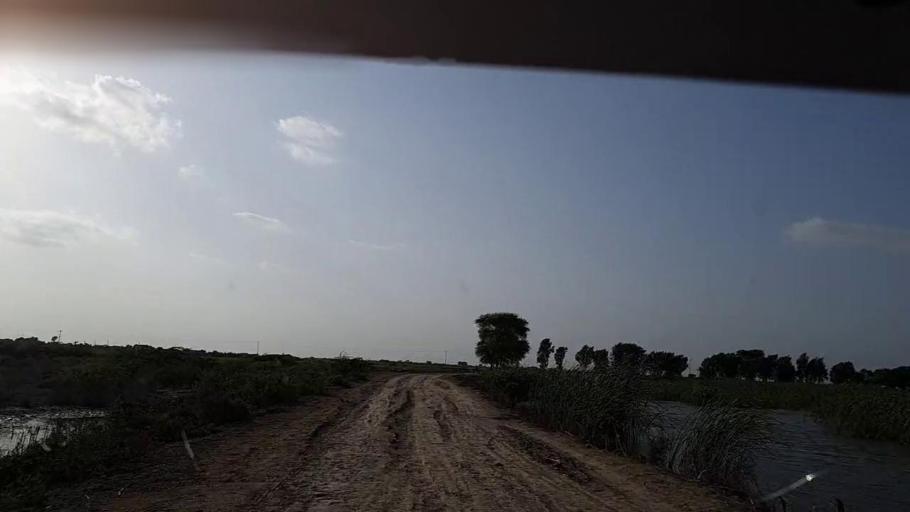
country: PK
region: Sindh
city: Badin
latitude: 24.5594
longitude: 68.8872
